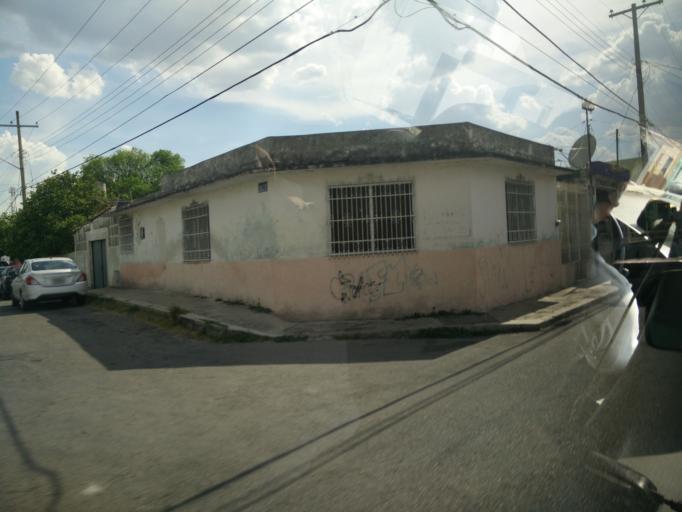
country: MX
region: Yucatan
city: Merida
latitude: 20.9649
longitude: -89.6026
